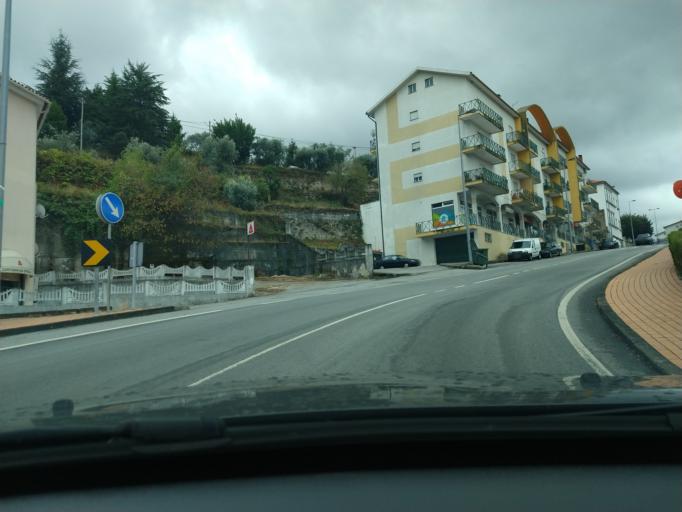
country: PT
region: Guarda
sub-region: Seia
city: Seia
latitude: 40.4027
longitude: -7.7113
